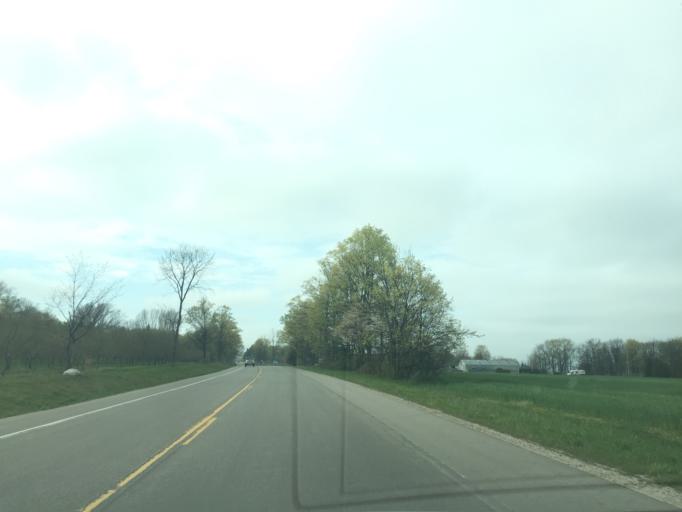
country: US
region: Michigan
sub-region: Leelanau County
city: Leland
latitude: 45.0729
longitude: -85.5886
